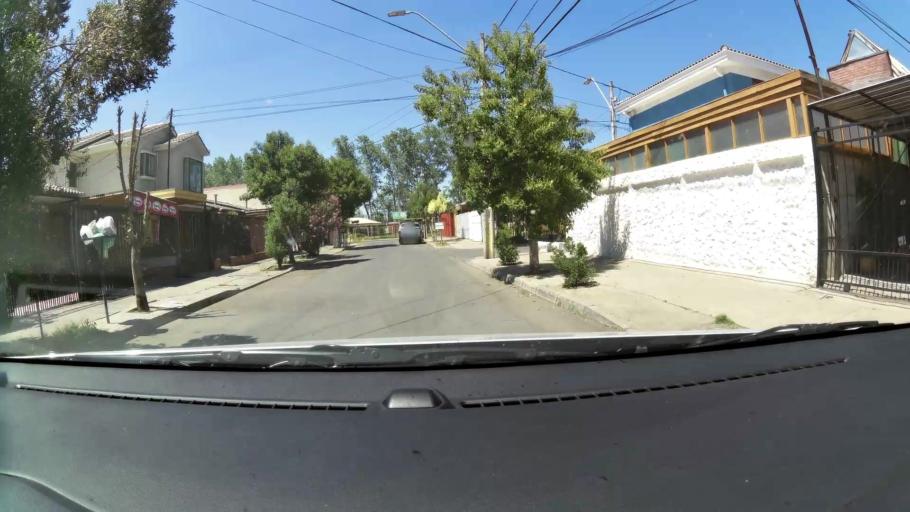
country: CL
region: Santiago Metropolitan
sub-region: Provincia de Maipo
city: San Bernardo
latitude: -33.6244
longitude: -70.7117
